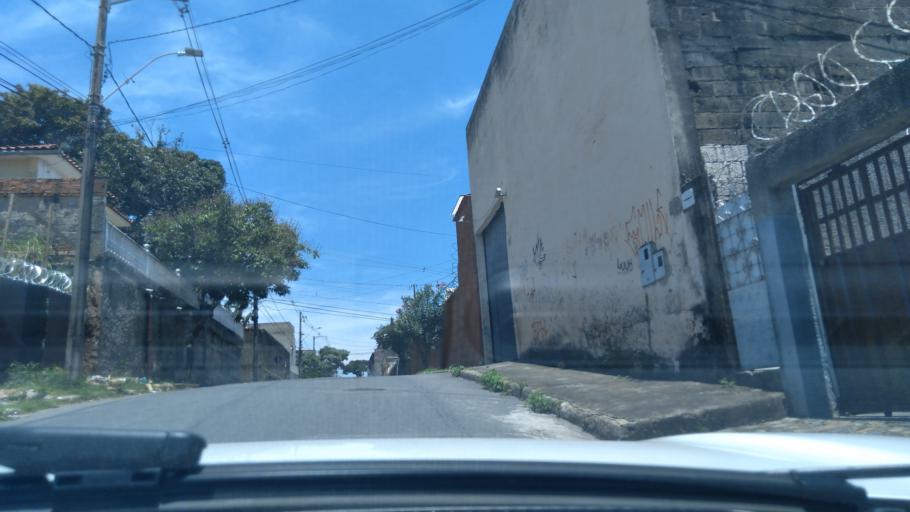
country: BR
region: Minas Gerais
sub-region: Contagem
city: Contagem
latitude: -19.9350
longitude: -44.0020
